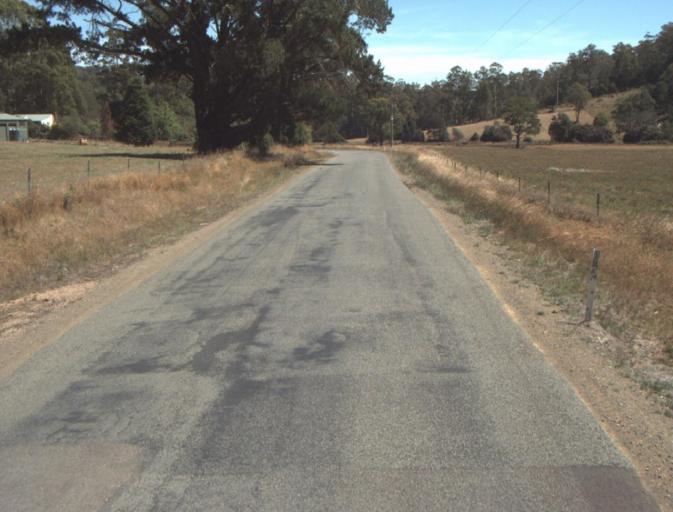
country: AU
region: Tasmania
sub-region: Dorset
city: Scottsdale
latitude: -41.3098
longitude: 147.3945
